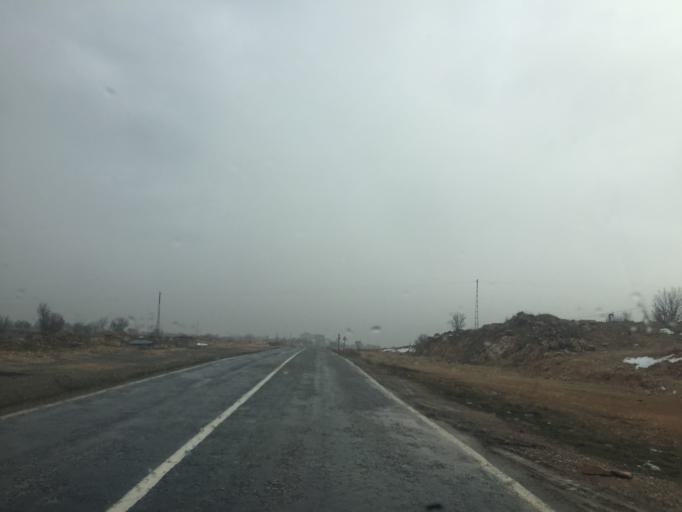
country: TR
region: Mardin
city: Omerli
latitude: 37.3950
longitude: 40.9221
